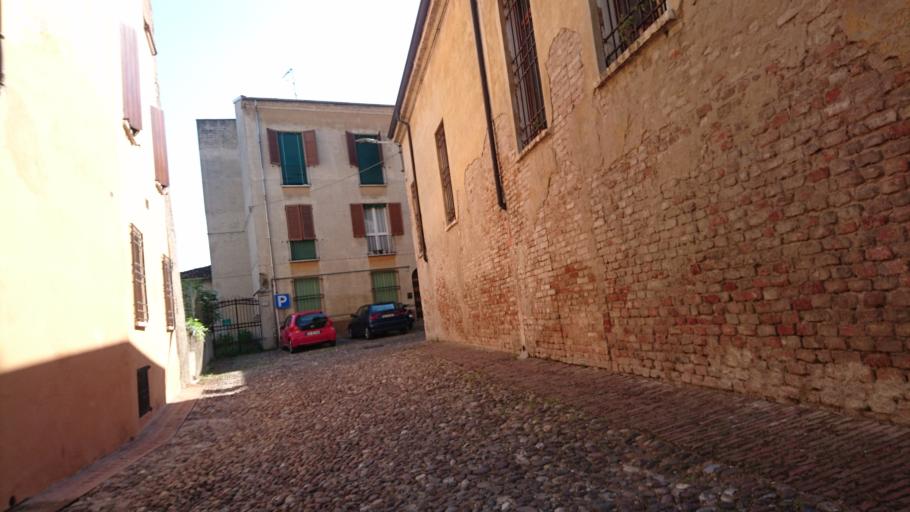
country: IT
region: Lombardy
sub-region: Provincia di Mantova
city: Mantova
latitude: 45.1620
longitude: 10.7981
